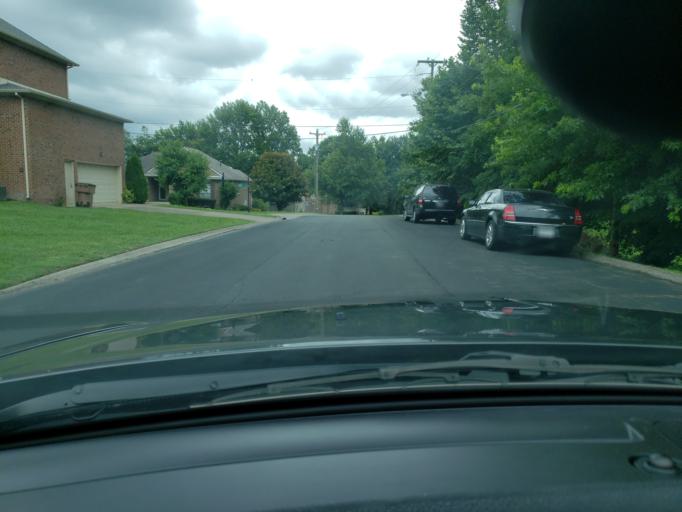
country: US
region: Tennessee
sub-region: Williamson County
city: Nolensville
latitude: 36.0355
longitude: -86.6807
